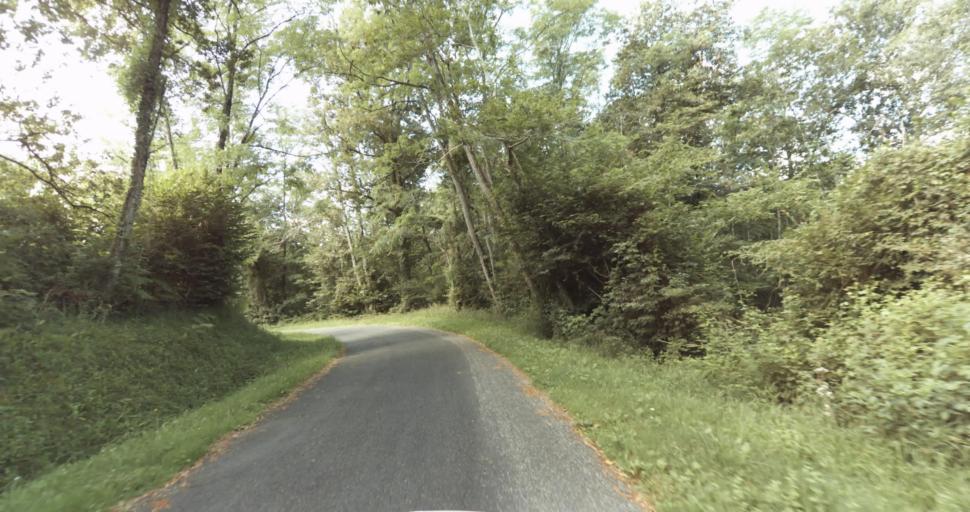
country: FR
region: Aquitaine
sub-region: Departement de la Gironde
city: Bazas
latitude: 44.4603
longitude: -0.2177
